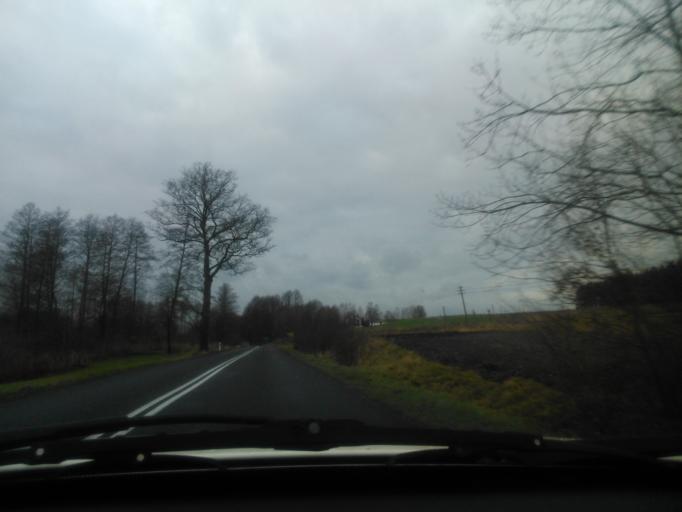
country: PL
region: Kujawsko-Pomorskie
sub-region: Powiat brodnicki
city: Bartniczka
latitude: 53.2468
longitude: 19.6248
